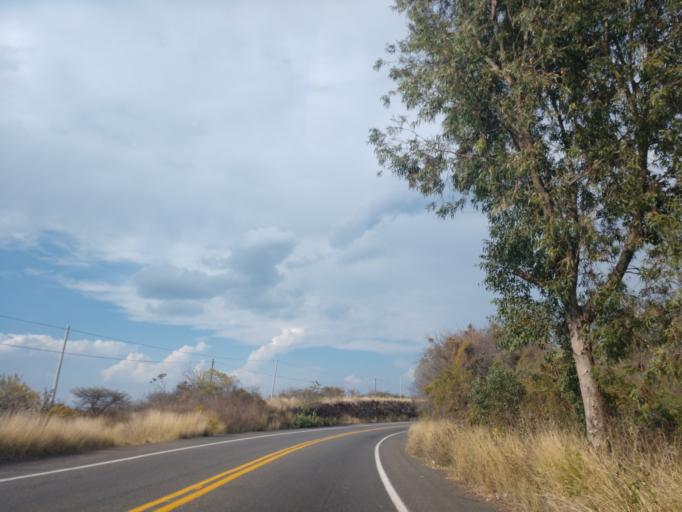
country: MX
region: Jalisco
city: La Manzanilla de la Paz
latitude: 20.0780
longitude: -103.1699
